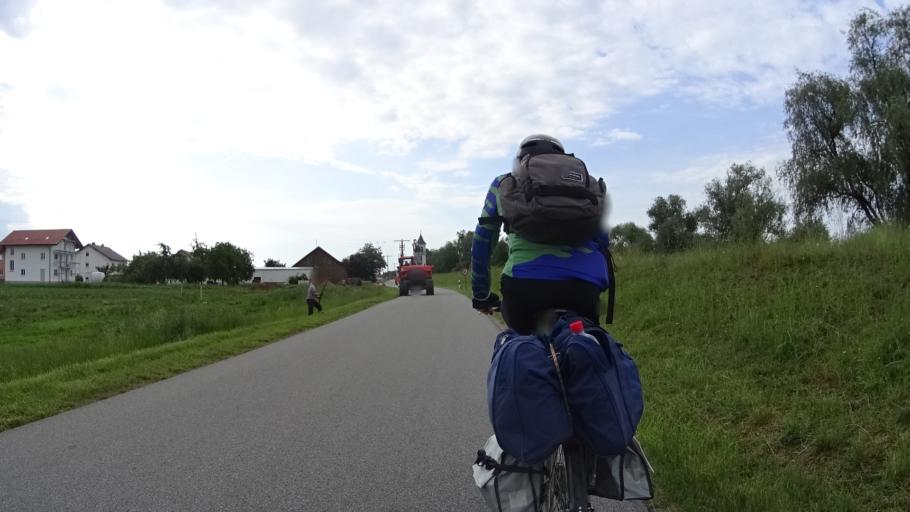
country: DE
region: Bavaria
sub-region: Lower Bavaria
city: Irlbach
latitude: 48.8716
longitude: 12.7562
